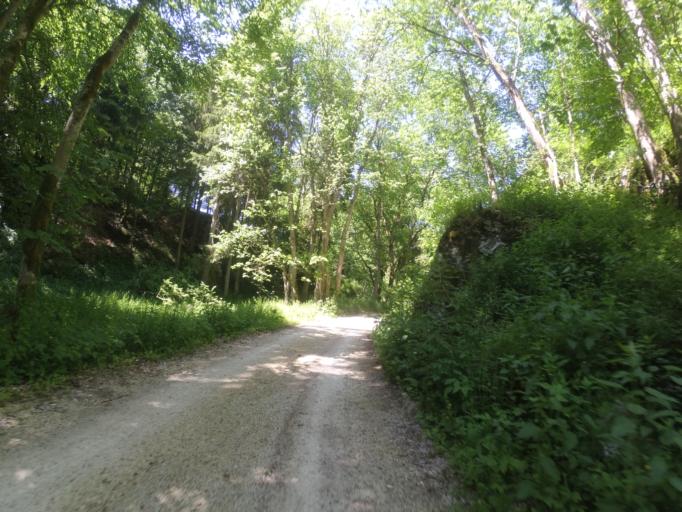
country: DE
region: Baden-Wuerttemberg
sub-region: Tuebingen Region
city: Berghulen
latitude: 48.4805
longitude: 9.8056
